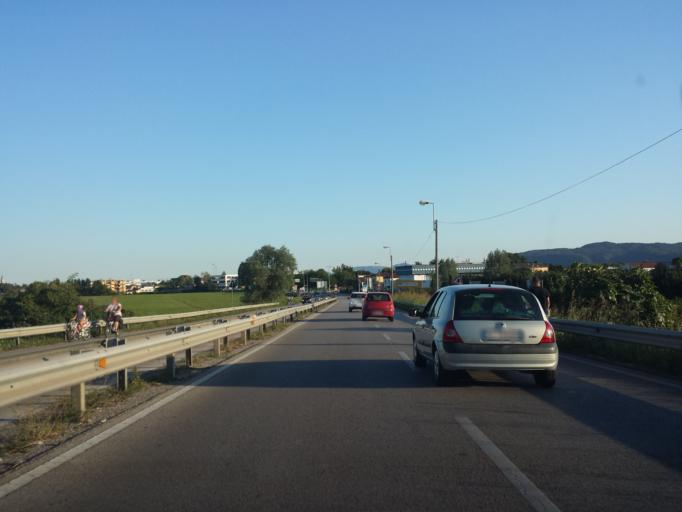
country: IT
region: Veneto
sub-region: Provincia di Vicenza
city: Villaggio Montegrappa
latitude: 45.5363
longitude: 11.5887
